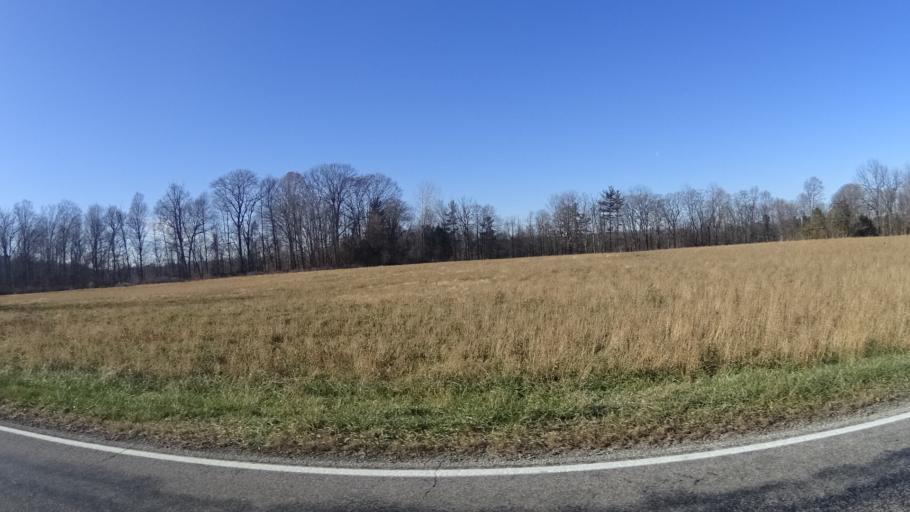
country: US
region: Ohio
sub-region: Lorain County
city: South Amherst
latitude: 41.3699
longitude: -82.3072
